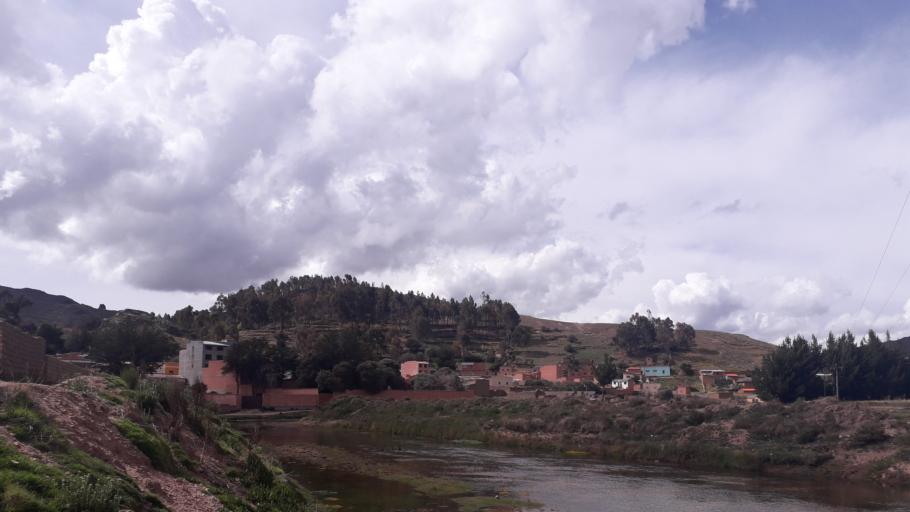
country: PE
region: Puno
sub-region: Moho
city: Putina
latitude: -15.5333
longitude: -69.2501
